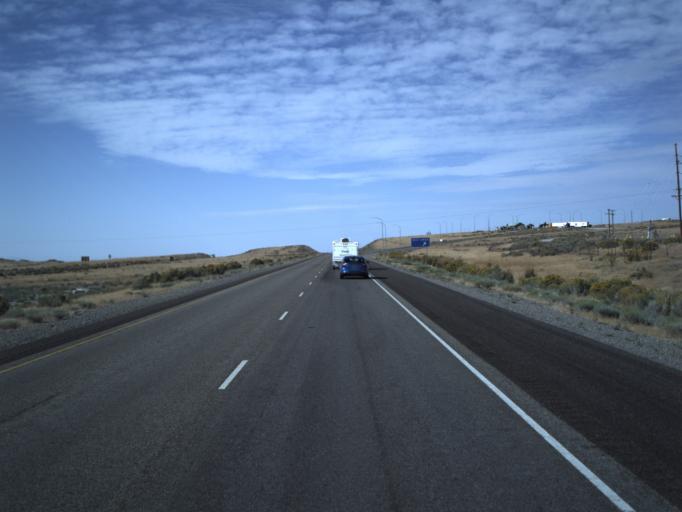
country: US
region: Utah
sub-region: Tooele County
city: Grantsville
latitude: 40.7633
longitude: -113.0016
